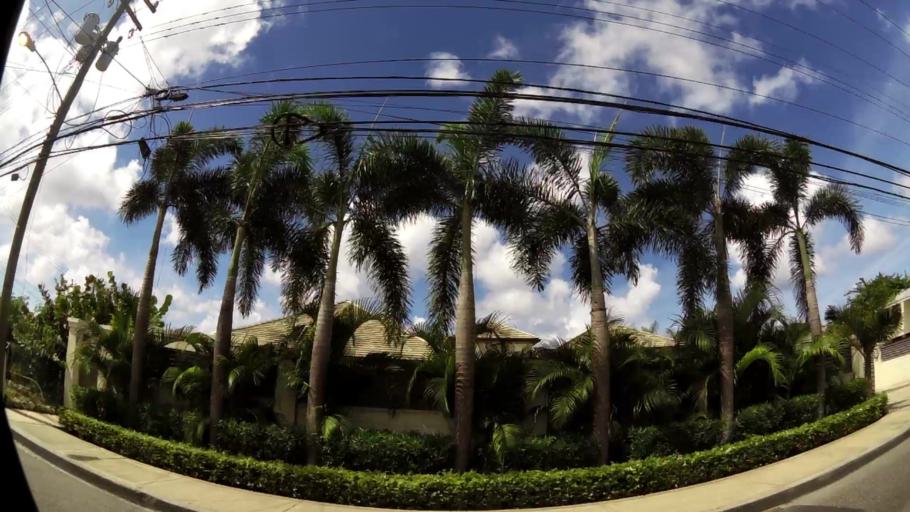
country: BB
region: Saint James
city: Holetown
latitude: 13.1518
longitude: -59.6375
